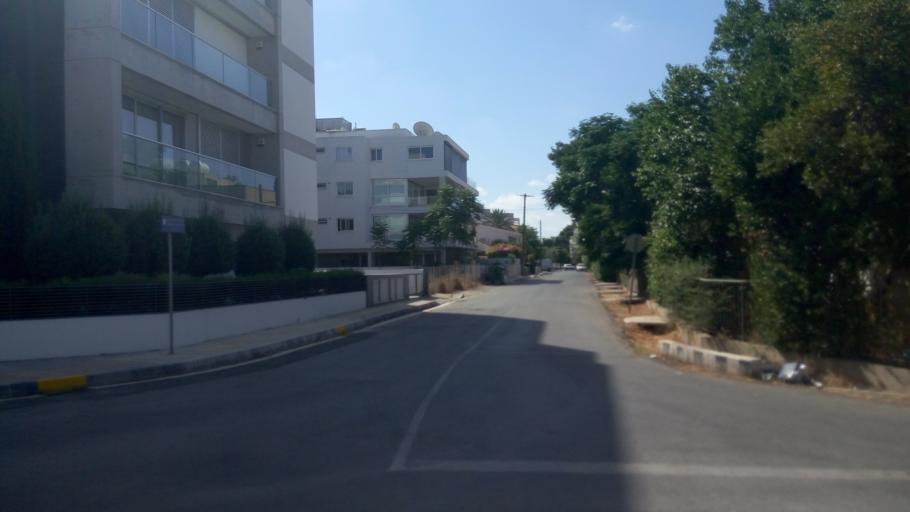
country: CY
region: Lefkosia
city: Nicosia
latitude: 35.1678
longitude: 33.3397
